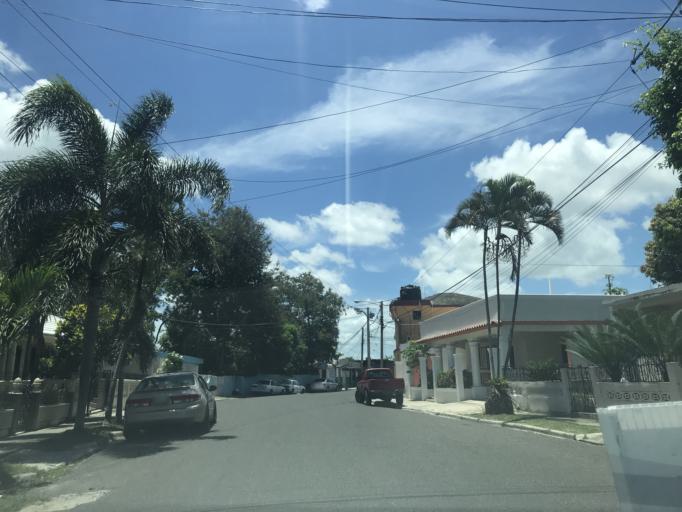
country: DO
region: Santiago
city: Santiago de los Caballeros
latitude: 19.4394
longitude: -70.6947
